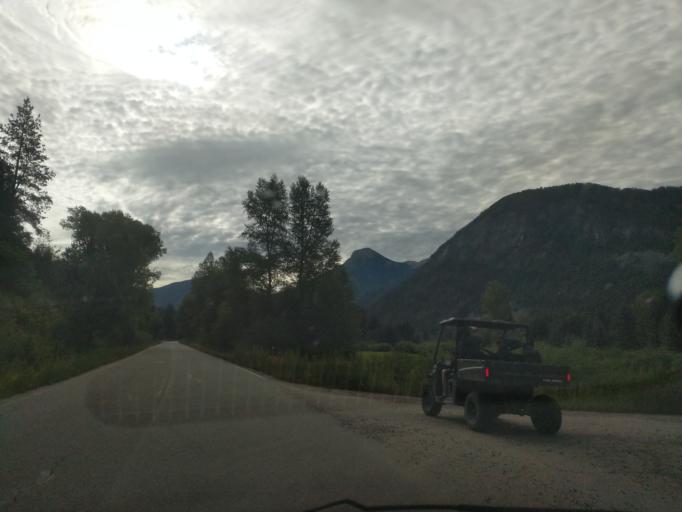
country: US
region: Colorado
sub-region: Gunnison County
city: Crested Butte
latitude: 39.0761
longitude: -107.2216
